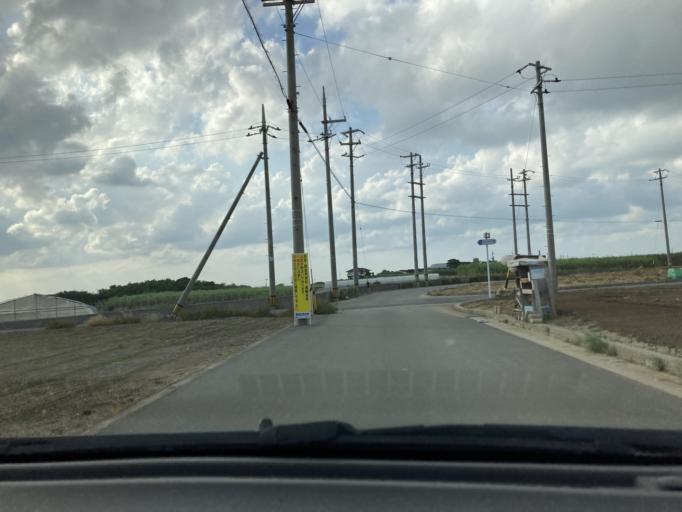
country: JP
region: Okinawa
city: Itoman
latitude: 26.0841
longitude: 127.6665
